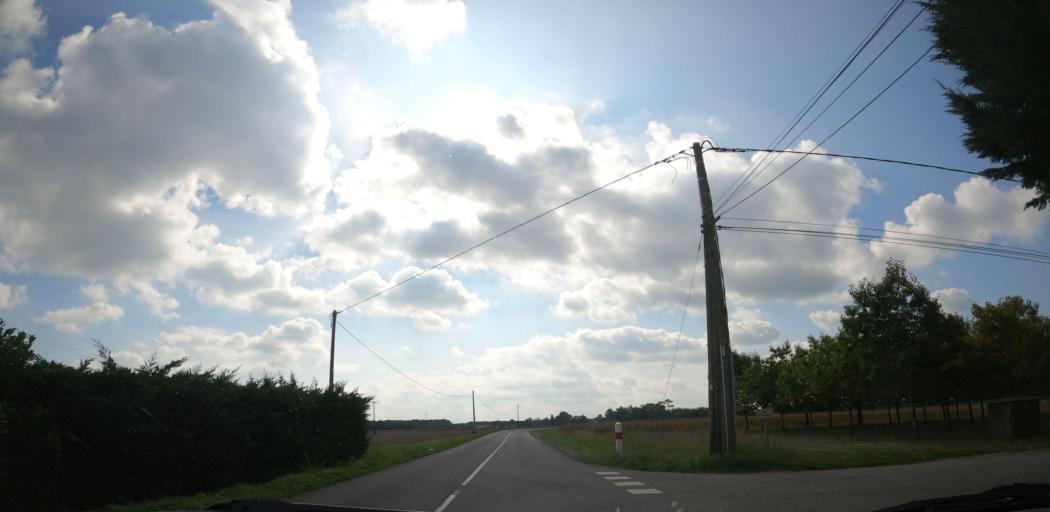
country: FR
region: Aquitaine
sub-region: Departement des Landes
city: Soustons
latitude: 43.7228
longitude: -1.3469
